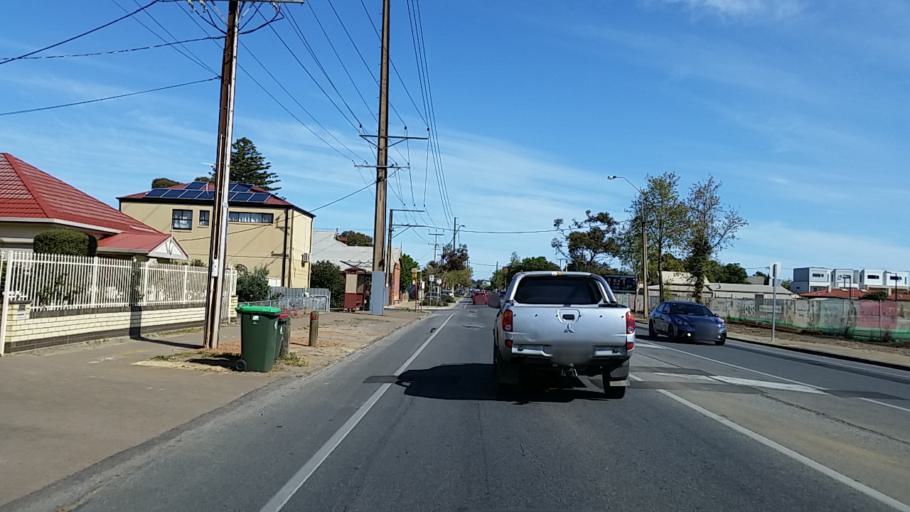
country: AU
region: South Australia
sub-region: Prospect
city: Prospect
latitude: -34.8771
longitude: 138.5843
